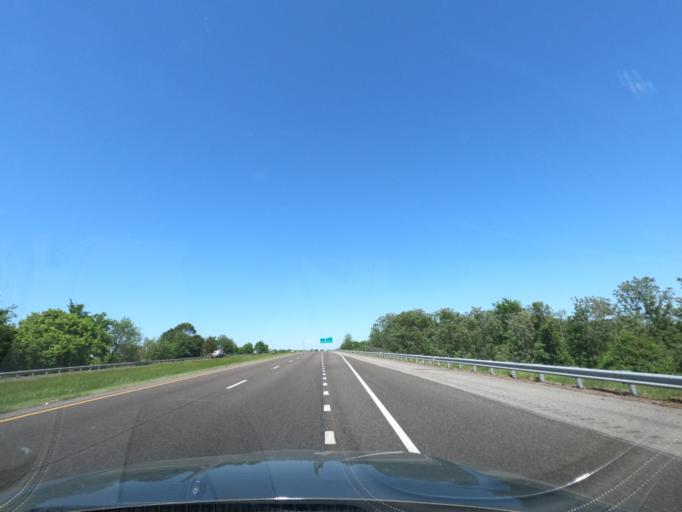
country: US
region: Georgia
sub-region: Richmond County
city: Augusta
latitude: 33.4464
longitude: -81.9363
